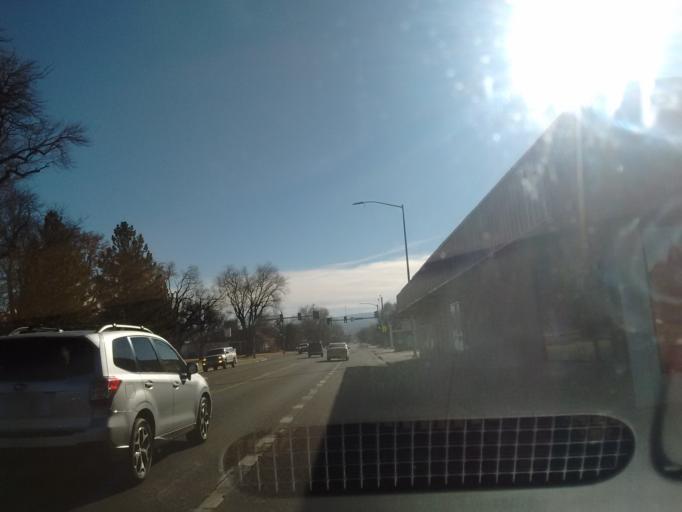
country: US
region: Colorado
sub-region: Mesa County
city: Grand Junction
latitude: 39.0742
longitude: -108.5524
